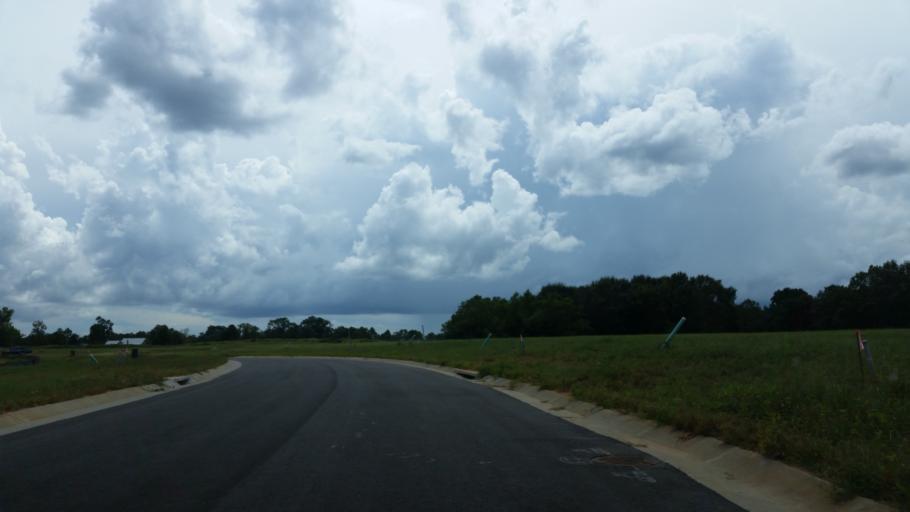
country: US
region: Florida
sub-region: Escambia County
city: Cantonment
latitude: 30.5397
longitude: -87.4114
